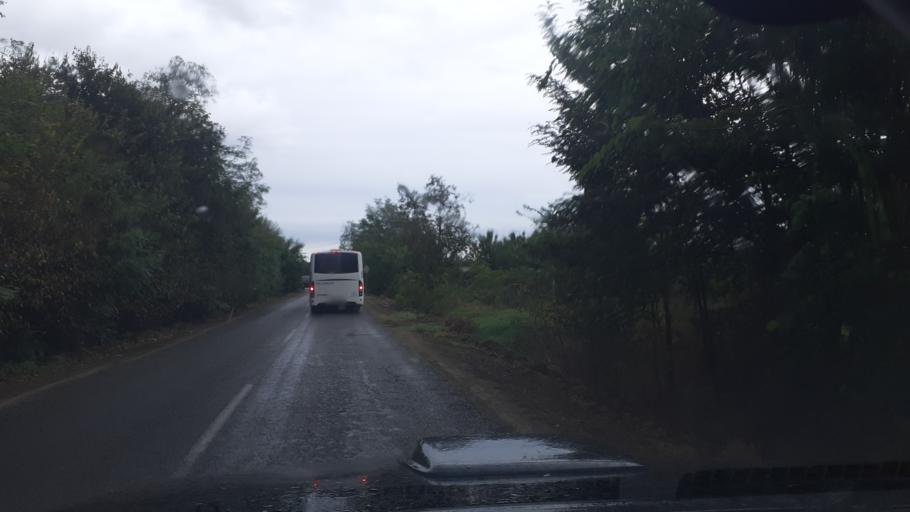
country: HU
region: Tolna
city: Bolcske
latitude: 46.7660
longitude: 18.9563
